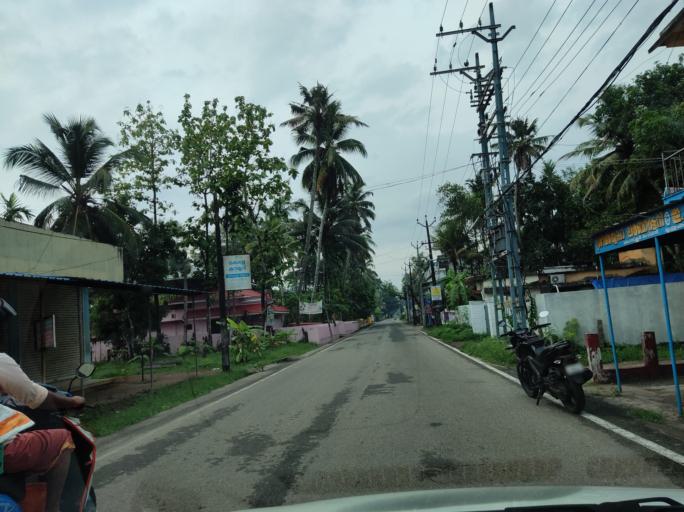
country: IN
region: Kerala
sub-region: Alappuzha
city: Kayankulam
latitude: 9.2118
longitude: 76.4614
